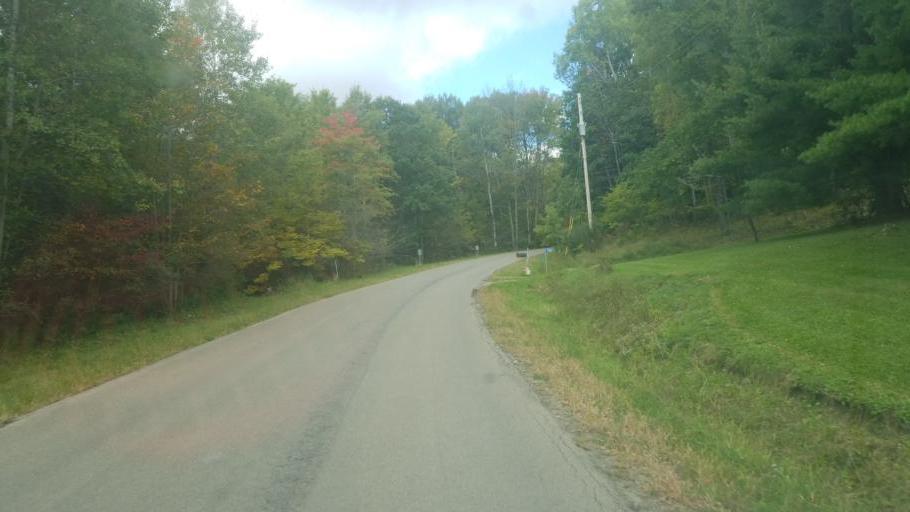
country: US
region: New York
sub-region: Cattaraugus County
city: Weston Mills
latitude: 42.1513
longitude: -78.3606
